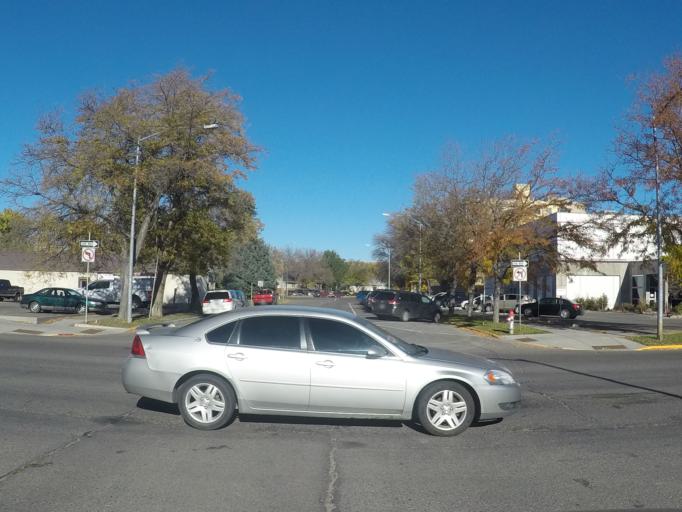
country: US
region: Montana
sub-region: Yellowstone County
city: Billings
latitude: 45.7816
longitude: -108.5144
